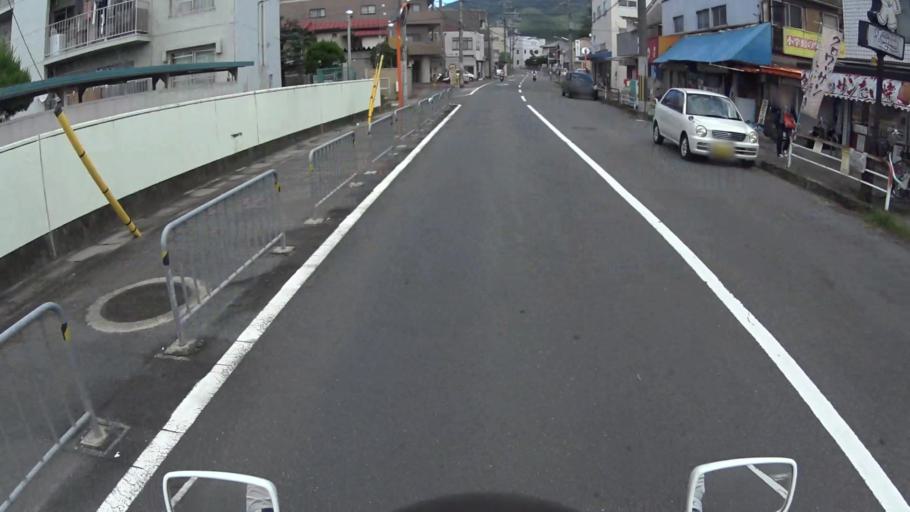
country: JP
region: Kyoto
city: Uji
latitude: 34.9433
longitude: 135.8132
